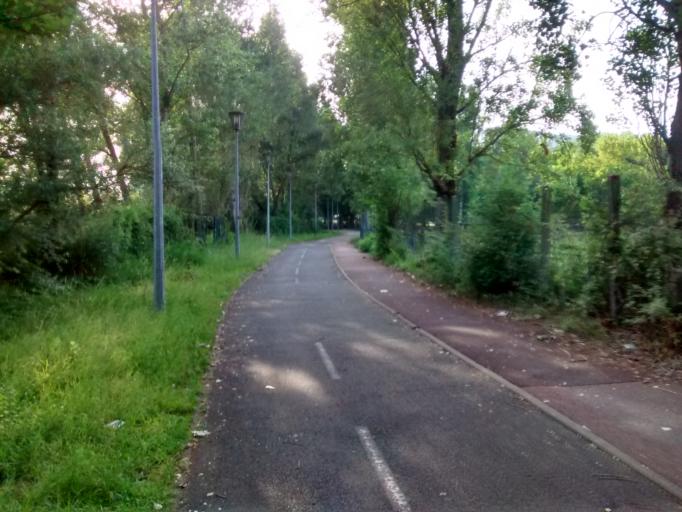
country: FR
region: Aquitaine
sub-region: Departement de la Gironde
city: Le Bouscat
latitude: 44.8706
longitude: -0.5681
